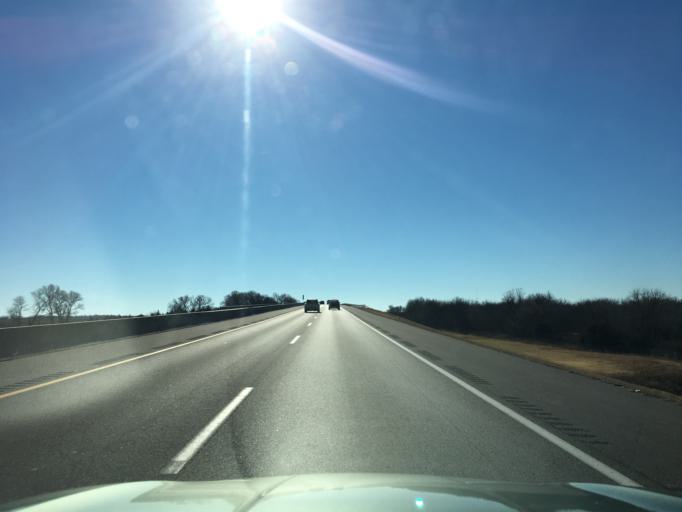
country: US
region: Kansas
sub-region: Sumner County
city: Belle Plaine
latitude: 37.3552
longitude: -97.3222
